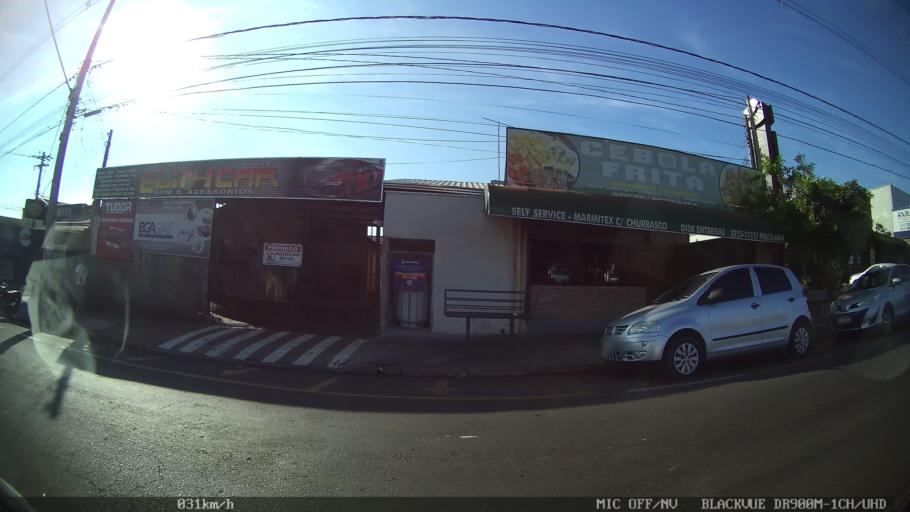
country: BR
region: Sao Paulo
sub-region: Sao Jose Do Rio Preto
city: Sao Jose do Rio Preto
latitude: -20.7881
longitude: -49.3437
